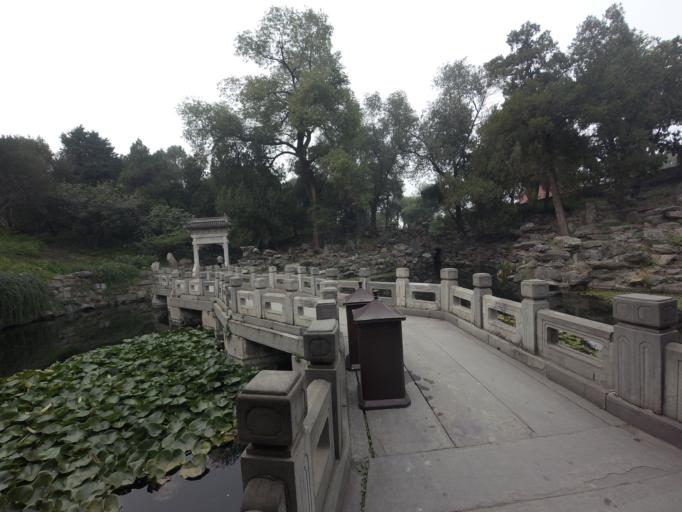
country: CN
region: Beijing
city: Jingshan
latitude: 39.9277
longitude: 116.3865
